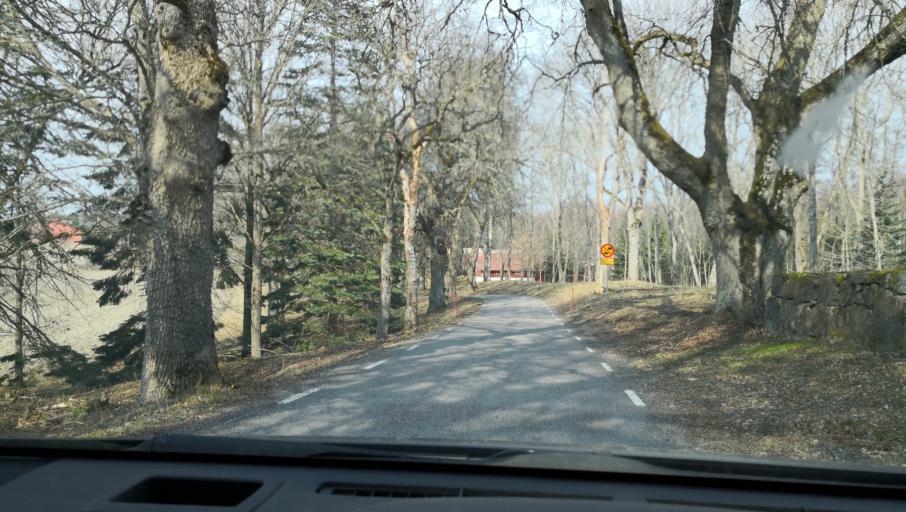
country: SE
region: OErebro
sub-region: Lindesbergs Kommun
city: Frovi
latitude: 59.4060
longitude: 15.4157
